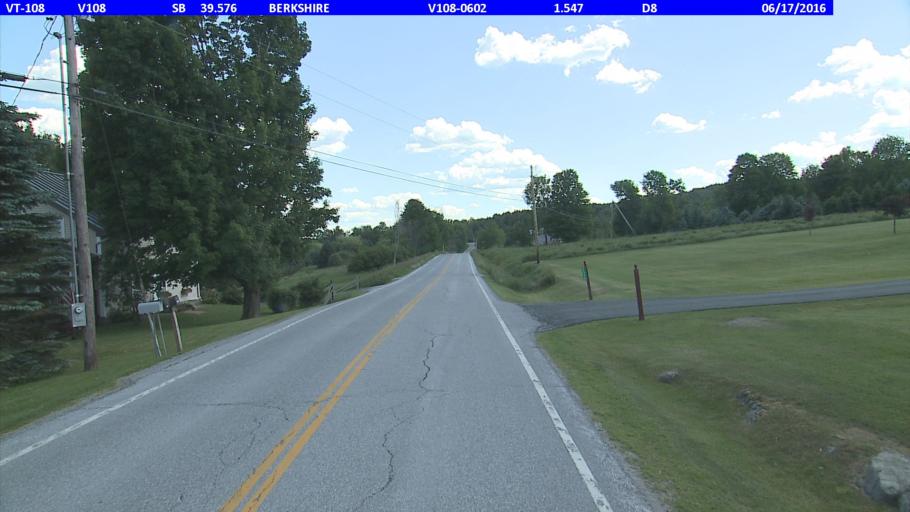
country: US
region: Vermont
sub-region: Franklin County
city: Enosburg Falls
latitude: 44.9469
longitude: -72.8132
